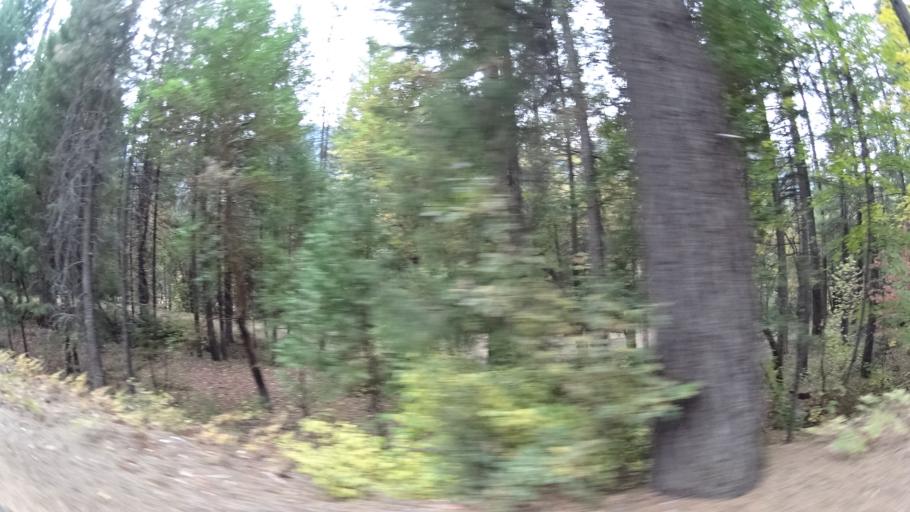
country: US
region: California
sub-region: Siskiyou County
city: Happy Camp
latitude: 41.8632
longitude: -123.4022
